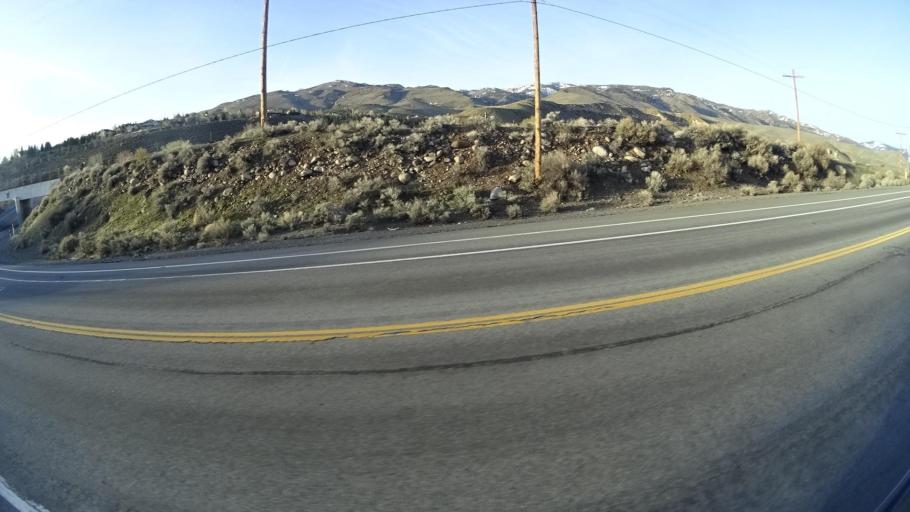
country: US
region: Nevada
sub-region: Washoe County
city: Mogul
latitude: 39.5083
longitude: -119.8894
